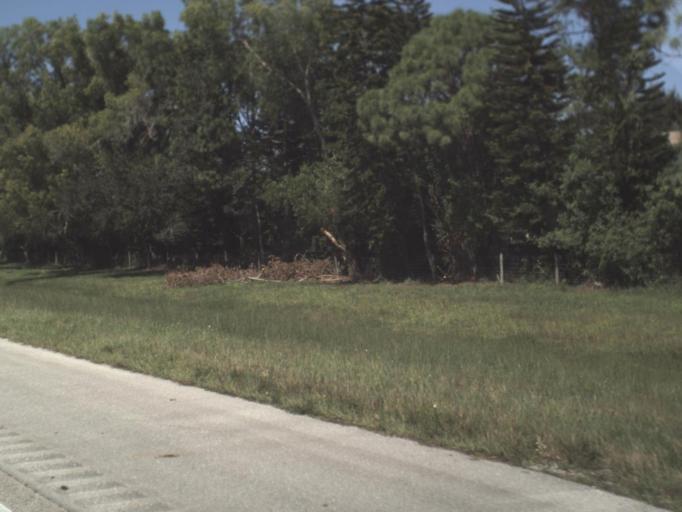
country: US
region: Florida
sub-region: Collier County
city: Golden Gate
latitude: 26.1667
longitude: -81.7271
